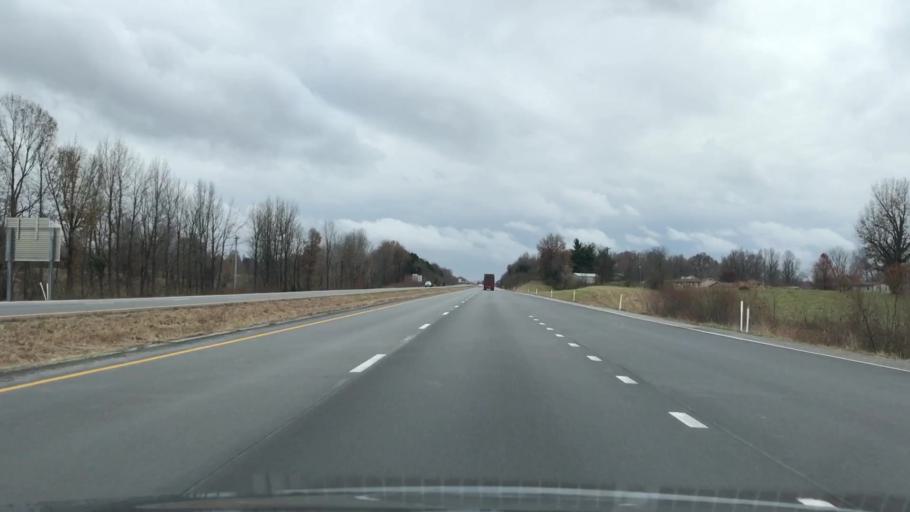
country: US
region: Kentucky
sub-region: Hopkins County
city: Madisonville
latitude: 37.4123
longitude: -87.4735
